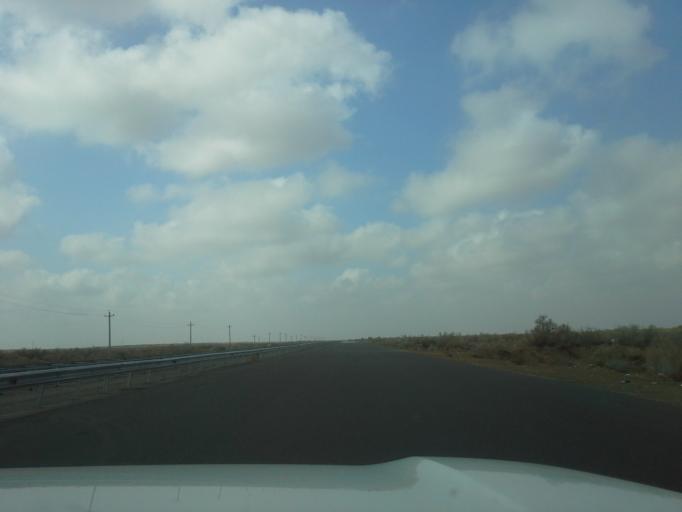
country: TM
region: Mary
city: Mary
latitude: 37.4083
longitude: 61.5346
